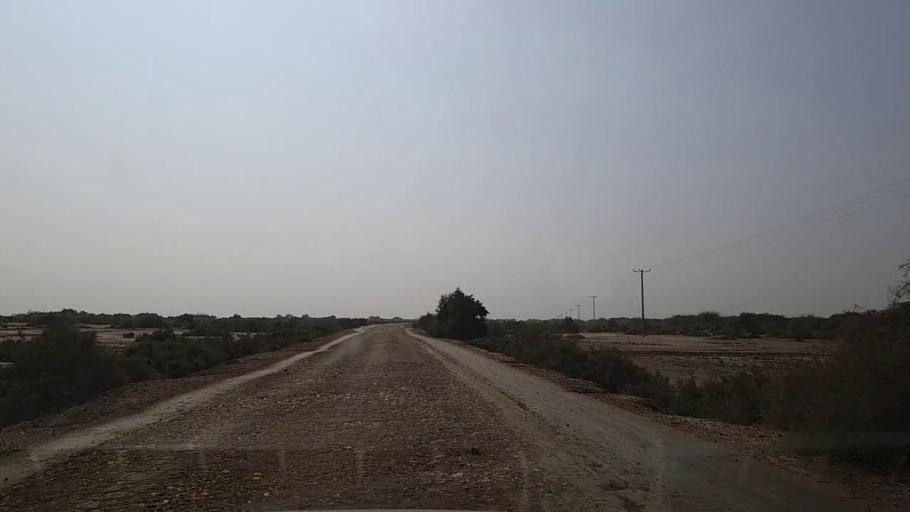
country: PK
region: Sindh
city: Mirpur Sakro
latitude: 24.5343
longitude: 67.5945
